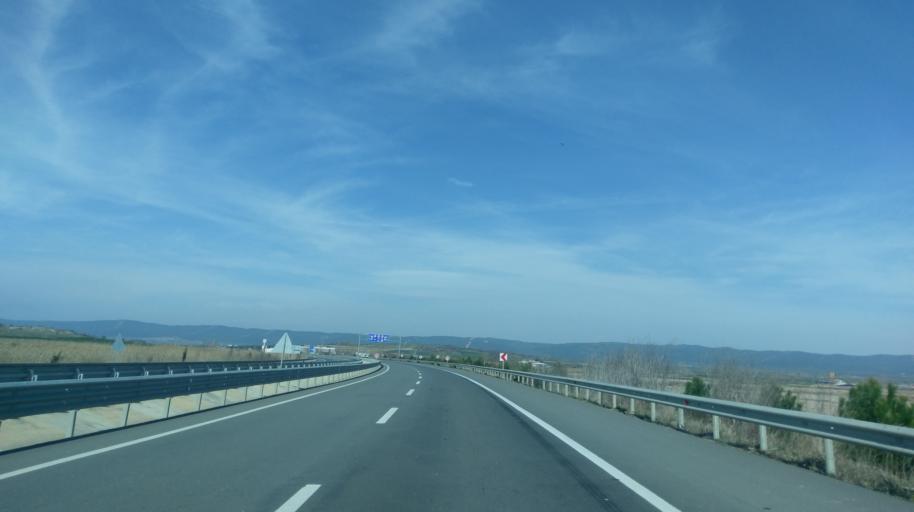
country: TR
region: Canakkale
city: Evrese
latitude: 40.6351
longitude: 26.8672
